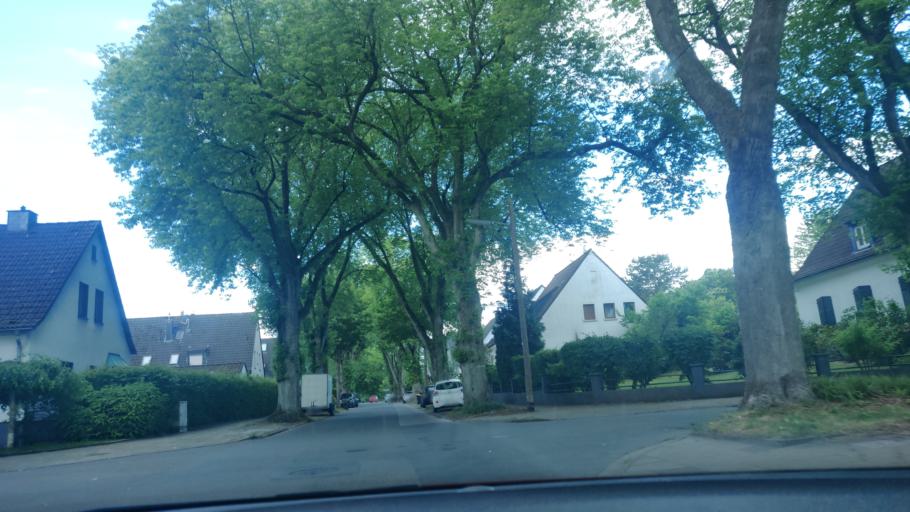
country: DE
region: North Rhine-Westphalia
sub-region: Regierungsbezirk Dusseldorf
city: Velbert
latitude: 51.3792
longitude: 7.0119
